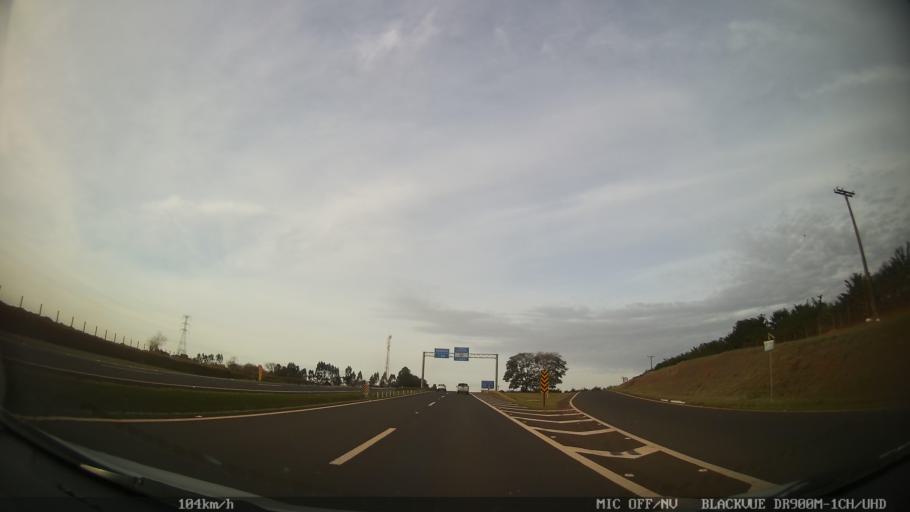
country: BR
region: Sao Paulo
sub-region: Iracemapolis
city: Iracemapolis
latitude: -22.6599
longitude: -47.5260
